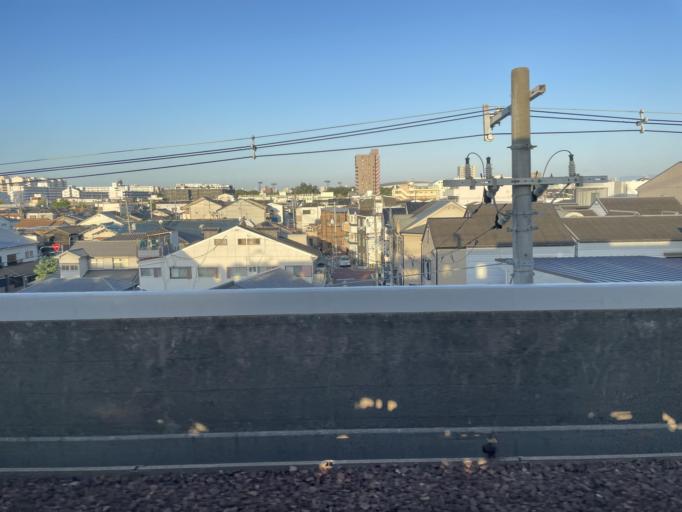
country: JP
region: Osaka
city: Matsubara
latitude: 34.6124
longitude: 135.5336
